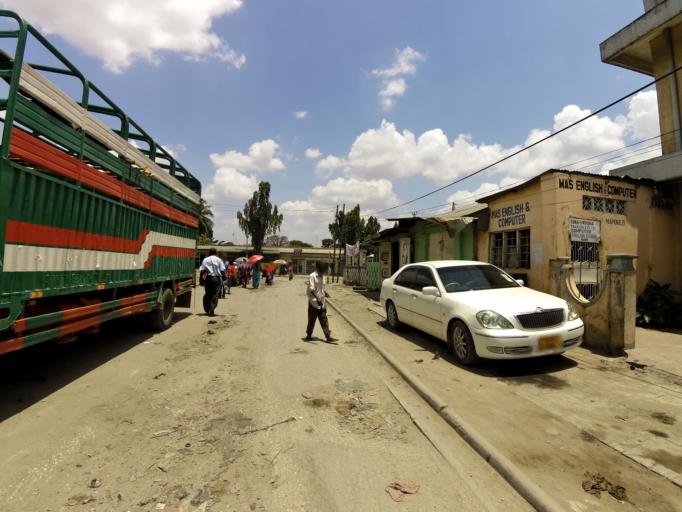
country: TZ
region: Dar es Salaam
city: Dar es Salaam
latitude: -6.8332
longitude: 39.2468
